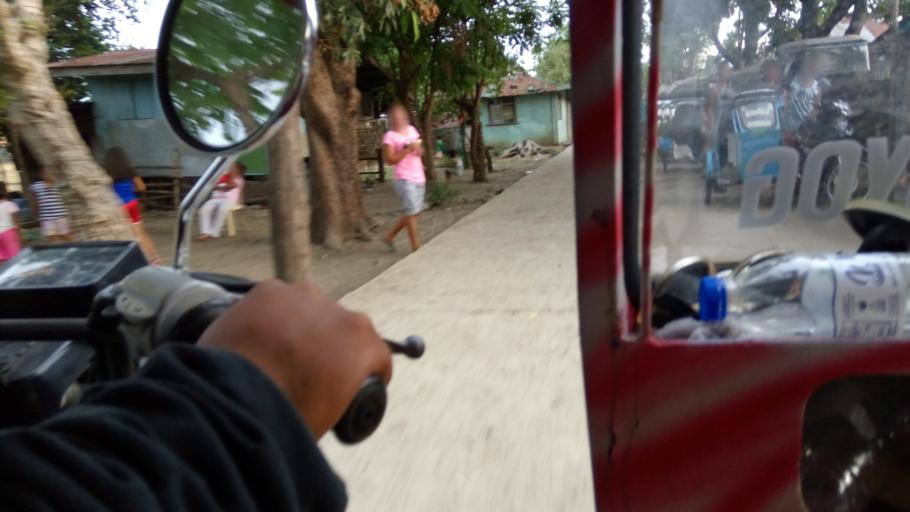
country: PH
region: Ilocos
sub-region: Province of La Union
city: Damortis
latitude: 16.2503
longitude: 120.4025
